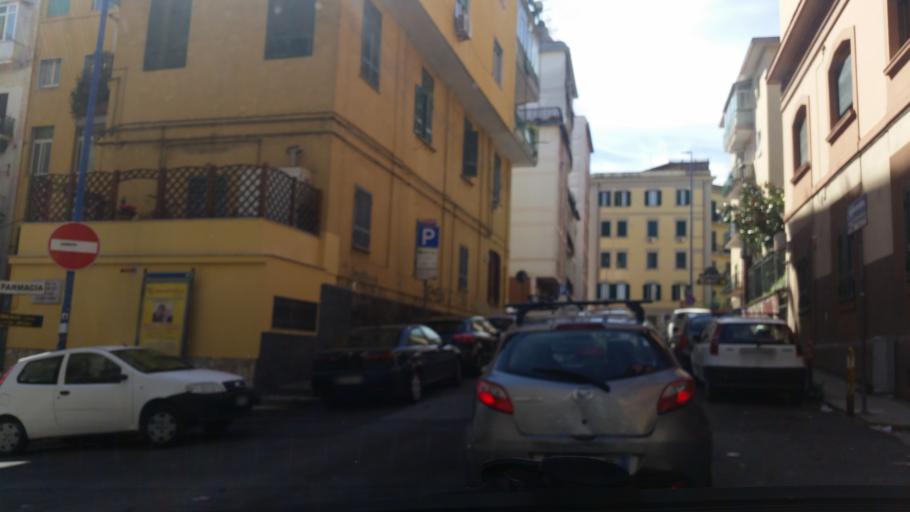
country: IT
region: Campania
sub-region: Provincia di Napoli
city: Napoli
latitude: 40.8545
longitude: 14.2337
